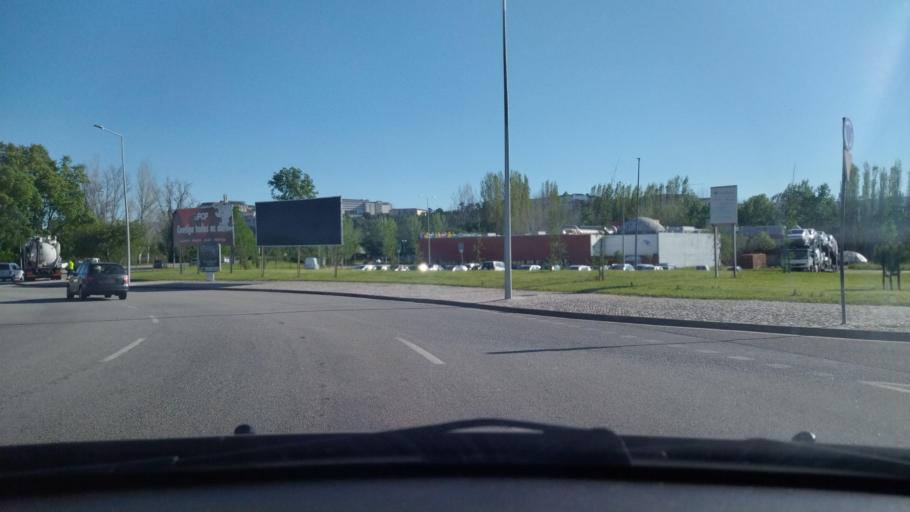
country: PT
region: Coimbra
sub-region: Coimbra
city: Coimbra
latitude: 40.1960
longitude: -8.4306
